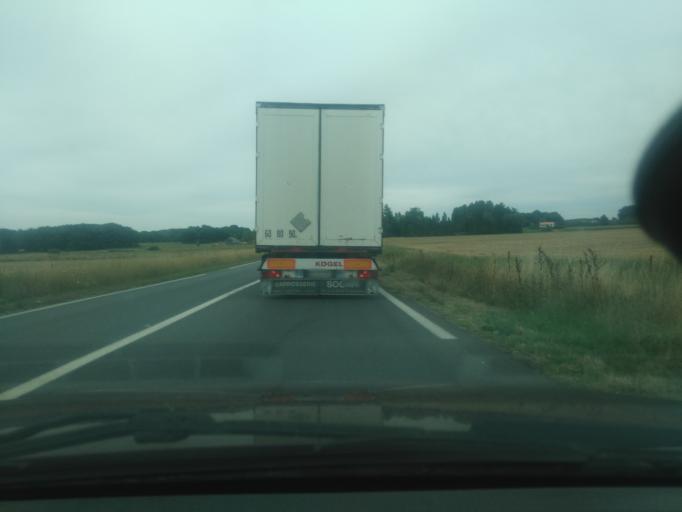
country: FR
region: Poitou-Charentes
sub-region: Departement de la Vienne
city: Sevres-Anxaumont
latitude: 46.5588
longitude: 0.4860
